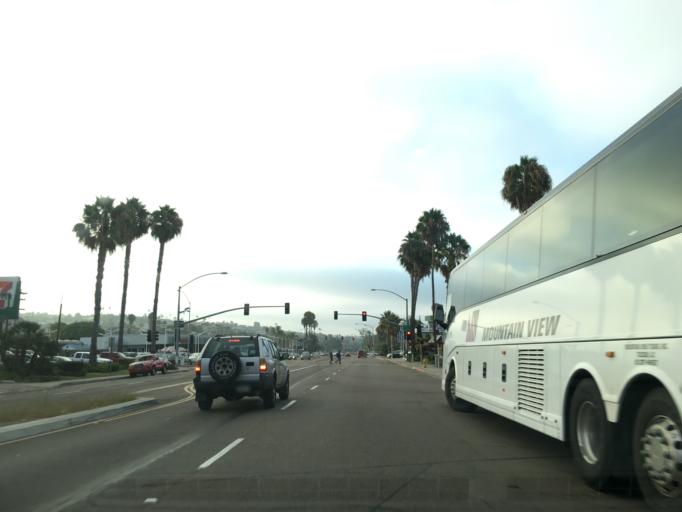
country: US
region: California
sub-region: San Diego County
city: La Jolla
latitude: 32.8033
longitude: -117.2171
